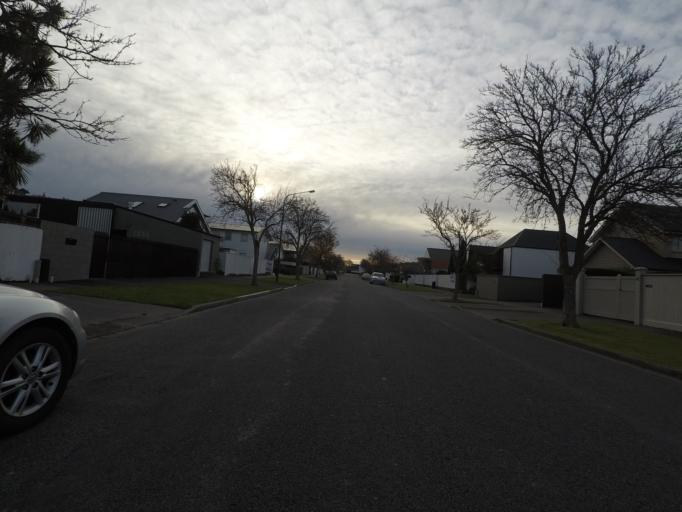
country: NZ
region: Canterbury
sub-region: Christchurch City
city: Christchurch
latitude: -43.5195
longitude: 172.6199
